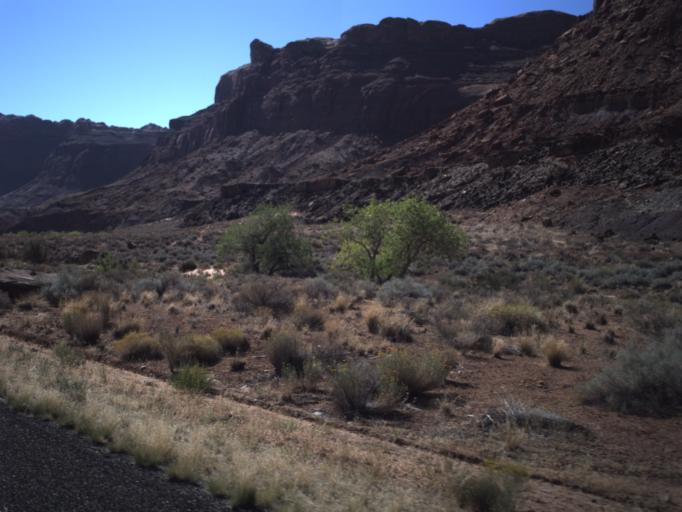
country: US
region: Utah
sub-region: San Juan County
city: Blanding
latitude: 37.9173
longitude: -110.4620
